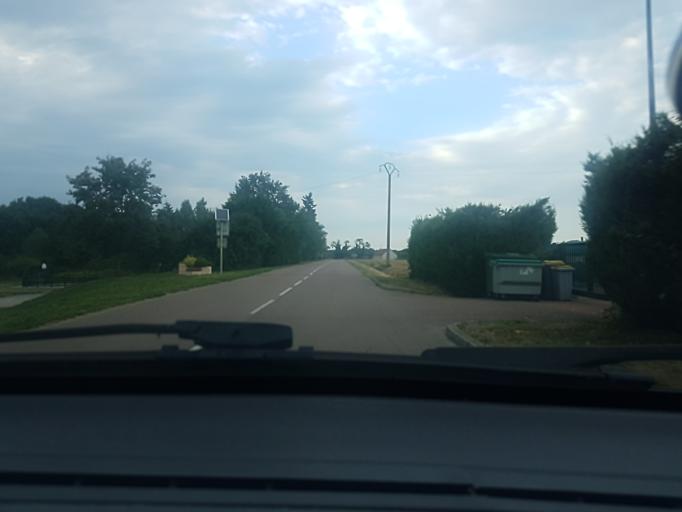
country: FR
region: Bourgogne
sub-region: Departement de Saone-et-Loire
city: Buxy
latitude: 46.7304
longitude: 4.7490
